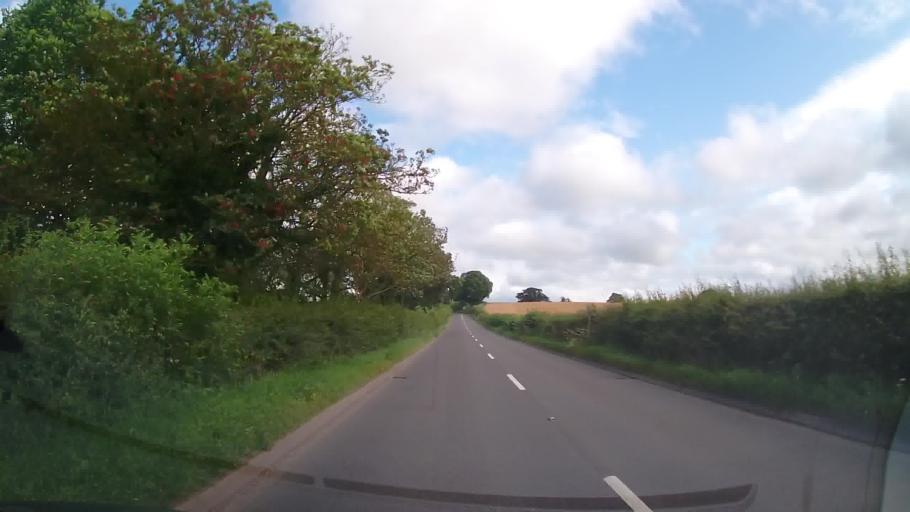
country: GB
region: England
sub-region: Shropshire
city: Pant
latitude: 52.7967
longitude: -3.0004
